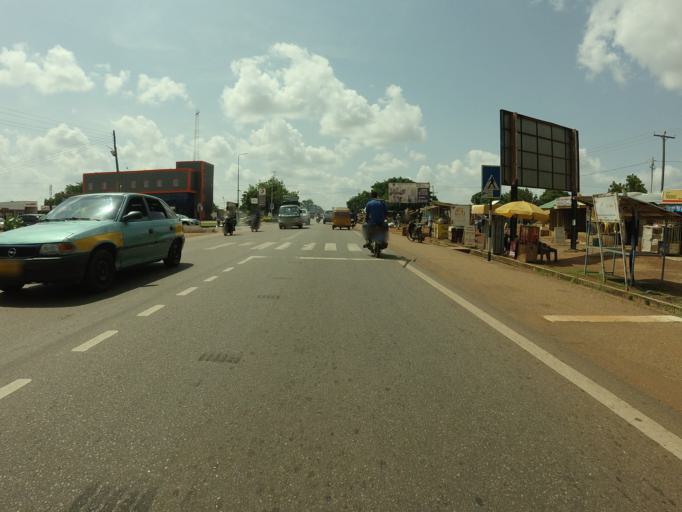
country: GH
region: Northern
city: Tamale
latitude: 9.4468
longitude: -0.8445
